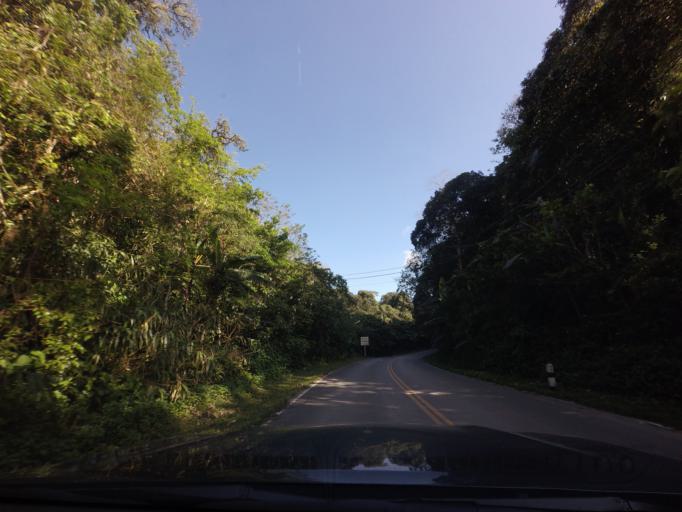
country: TH
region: Phetchabun
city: Lom Kao
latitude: 16.9015
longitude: 101.0851
